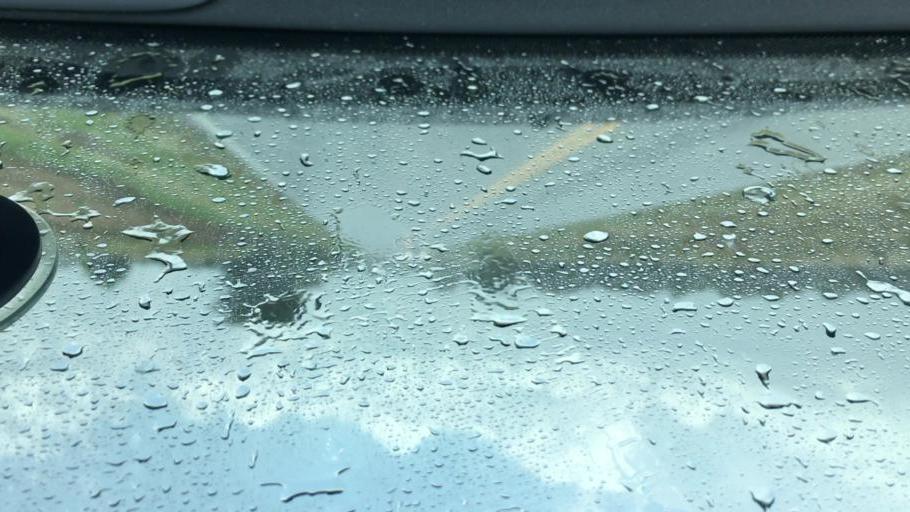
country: US
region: Oklahoma
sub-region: Johnston County
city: Tishomingo
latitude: 34.1773
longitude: -96.7143
